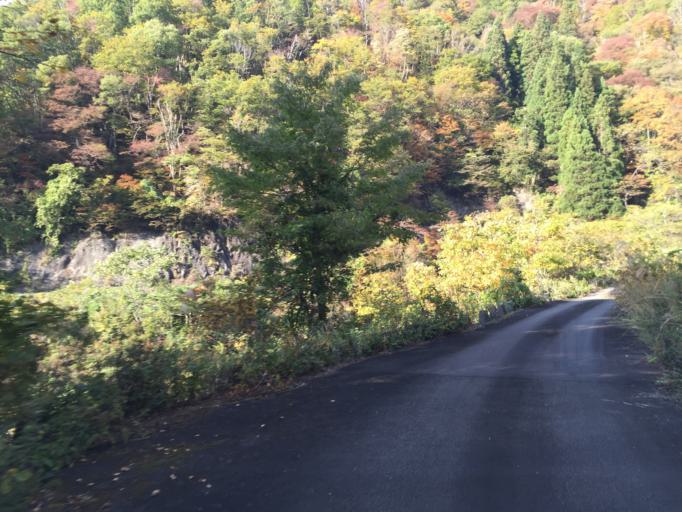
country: JP
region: Fukushima
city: Kitakata
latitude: 37.7480
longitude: 139.9262
